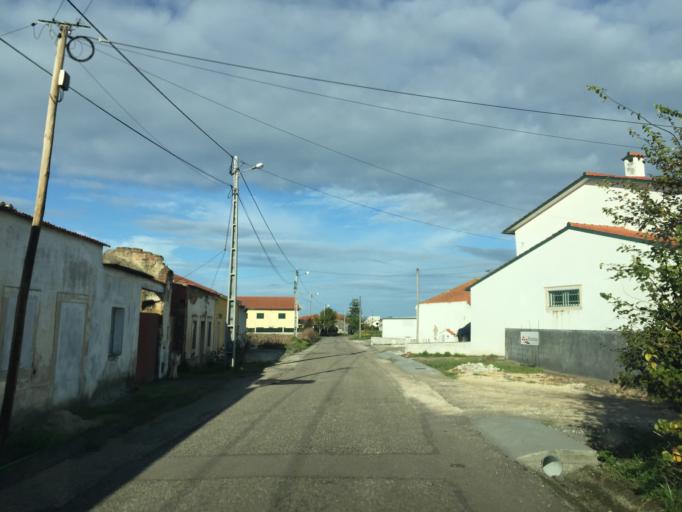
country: PT
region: Coimbra
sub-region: Figueira da Foz
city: Lavos
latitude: 40.0636
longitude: -8.8168
